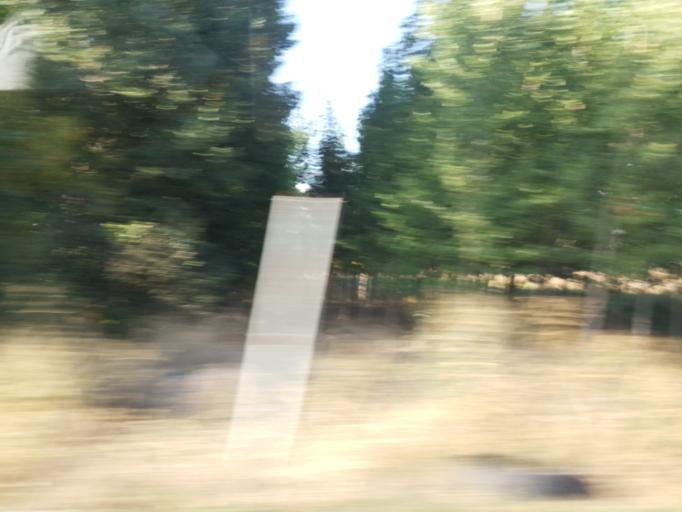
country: TR
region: Tokat
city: Yesilyurt
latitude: 40.0169
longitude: 36.2510
